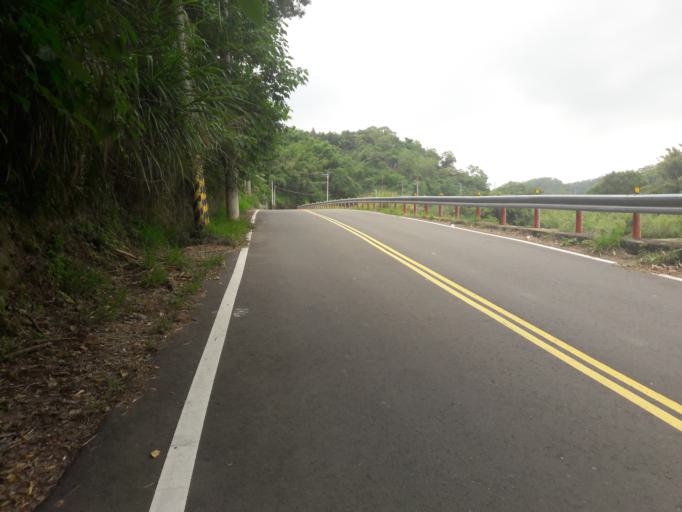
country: TW
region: Taiwan
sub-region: Hsinchu
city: Hsinchu
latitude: 24.7305
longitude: 120.9664
